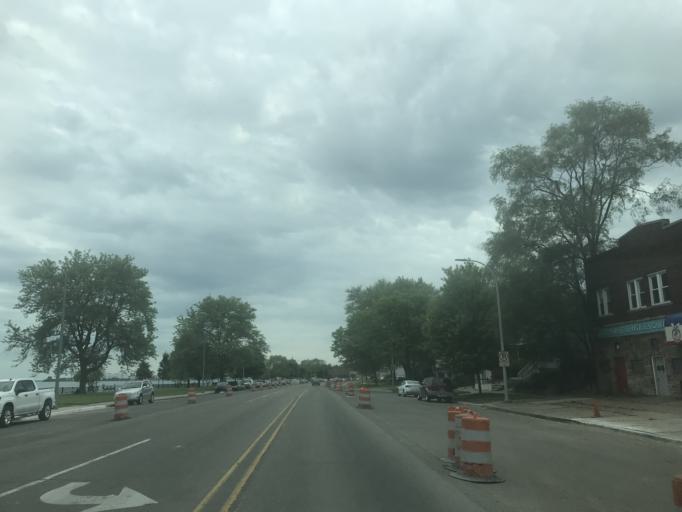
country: US
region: Michigan
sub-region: Wayne County
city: Ecorse
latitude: 42.2411
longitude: -83.1449
